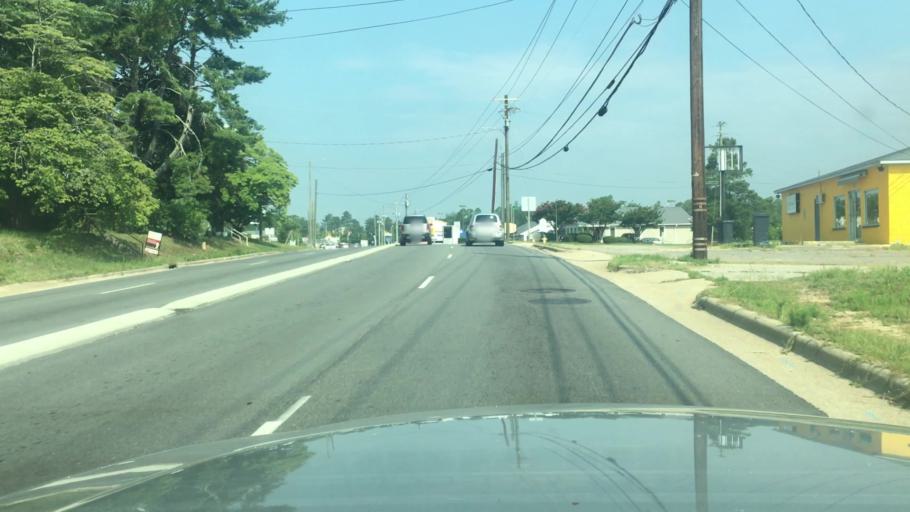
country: US
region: North Carolina
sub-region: Cumberland County
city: Hope Mills
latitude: 34.9771
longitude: -78.9528
